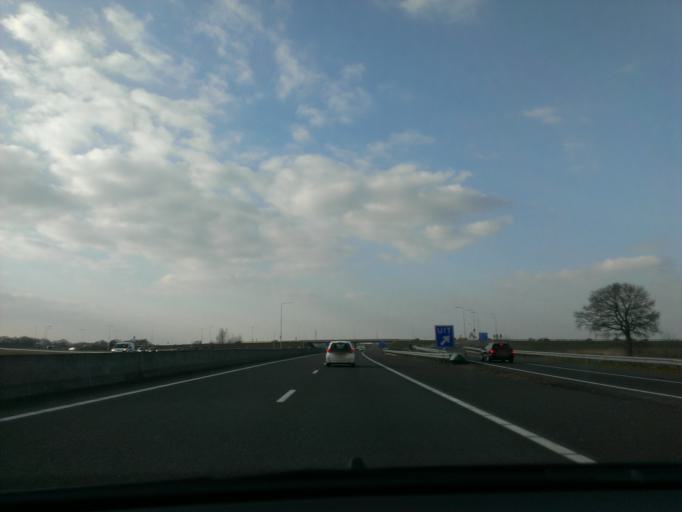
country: NL
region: Overijssel
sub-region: Gemeente Wierden
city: Wierden
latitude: 52.3393
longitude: 6.5992
